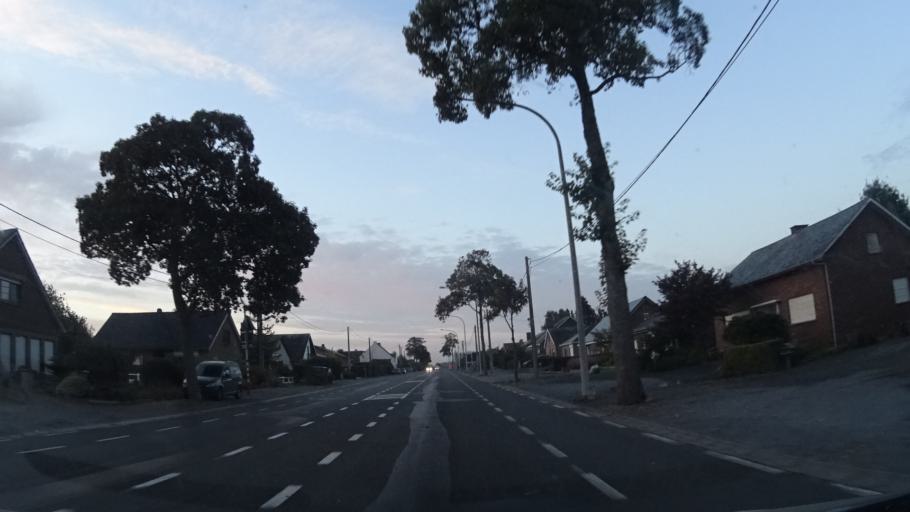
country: BE
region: Wallonia
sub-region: Province du Hainaut
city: Peruwelz
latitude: 50.5829
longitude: 3.6194
